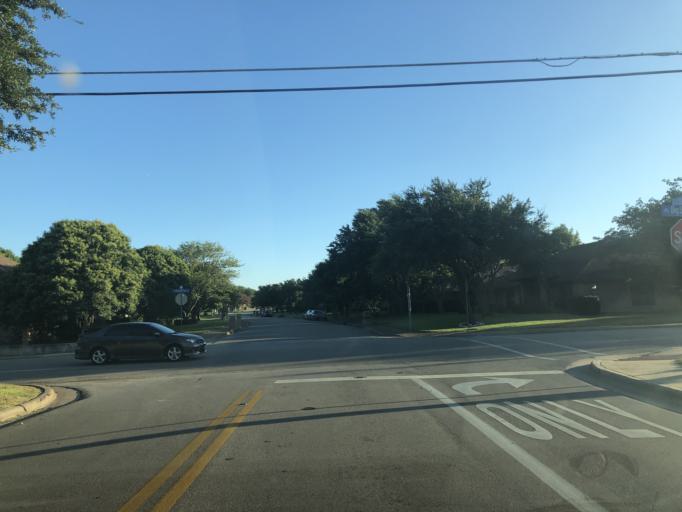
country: US
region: Texas
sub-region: Dallas County
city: Duncanville
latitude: 32.6419
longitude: -96.9335
